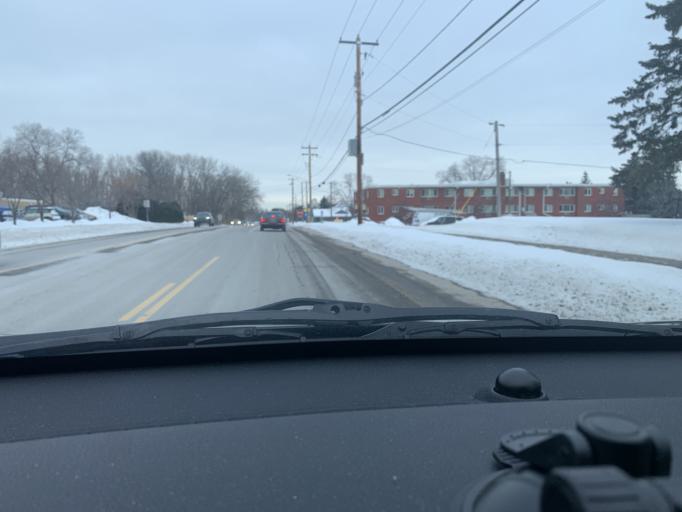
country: US
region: Minnesota
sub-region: Dakota County
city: South Saint Paul
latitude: 44.8893
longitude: -93.0703
